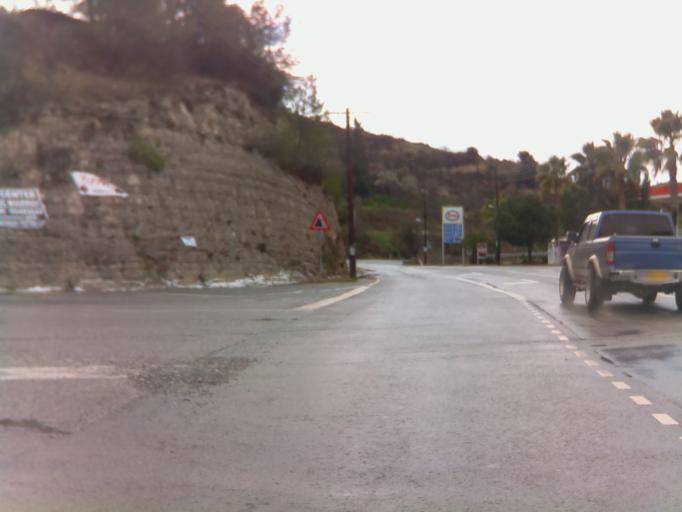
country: CY
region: Pafos
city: Tala
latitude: 34.8776
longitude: 32.4826
